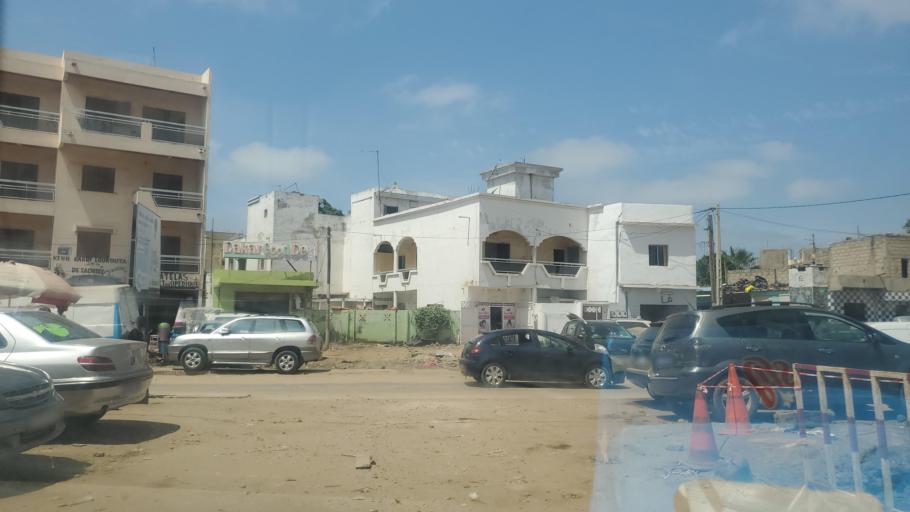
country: SN
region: Dakar
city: Grand Dakar
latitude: 14.7305
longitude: -17.4564
